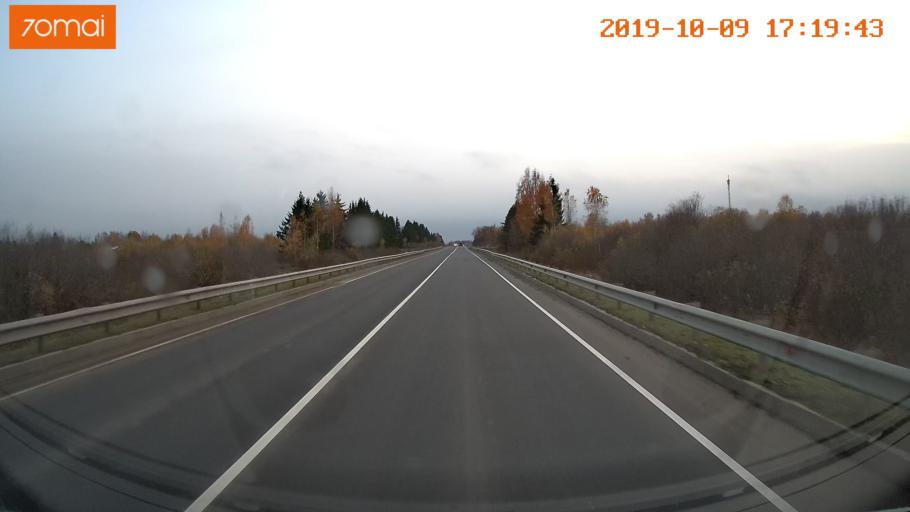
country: RU
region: Ivanovo
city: Furmanov
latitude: 57.2428
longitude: 41.1496
